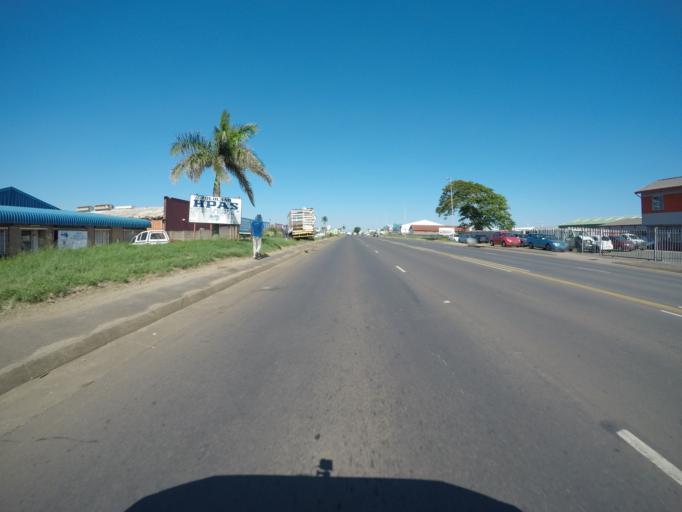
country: ZA
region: KwaZulu-Natal
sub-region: uThungulu District Municipality
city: Empangeni
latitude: -28.7773
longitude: 31.8955
